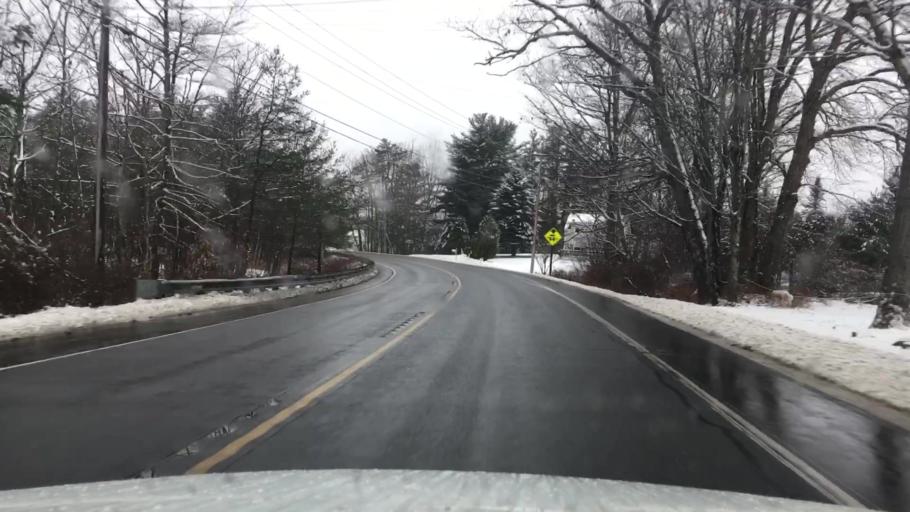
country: US
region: Maine
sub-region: Knox County
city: Rockport
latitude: 44.1773
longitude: -69.1275
